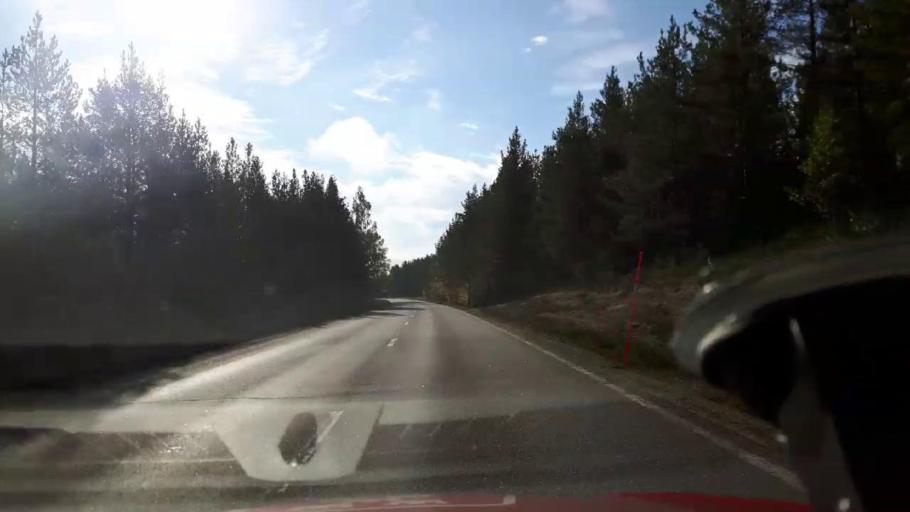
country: SE
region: Vaesternorrland
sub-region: Ange Kommun
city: Ange
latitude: 62.0695
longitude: 15.1044
